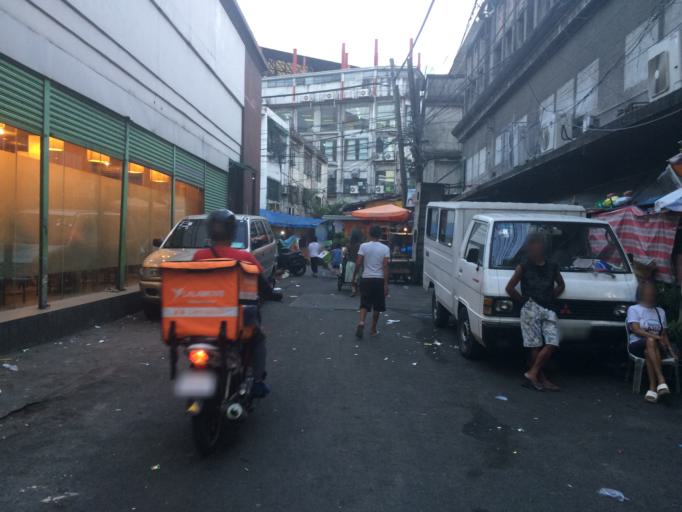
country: PH
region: Metro Manila
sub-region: City of Manila
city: Quiapo
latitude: 14.5981
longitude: 120.9816
